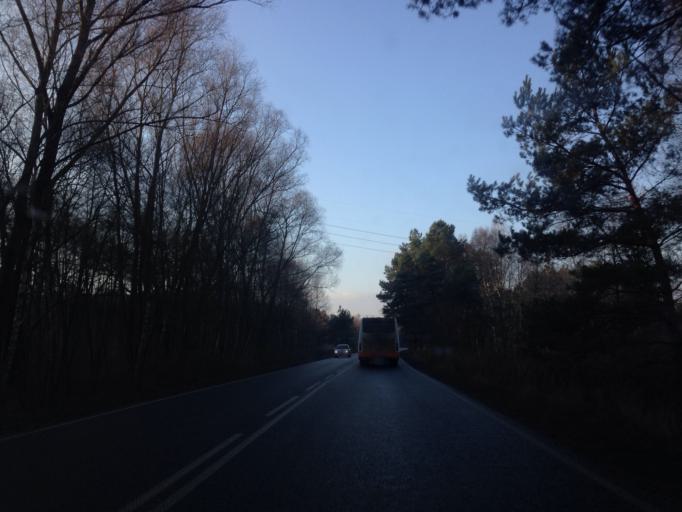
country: PL
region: Kujawsko-Pomorskie
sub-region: Bydgoszcz
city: Fordon
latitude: 53.0759
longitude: 18.1347
